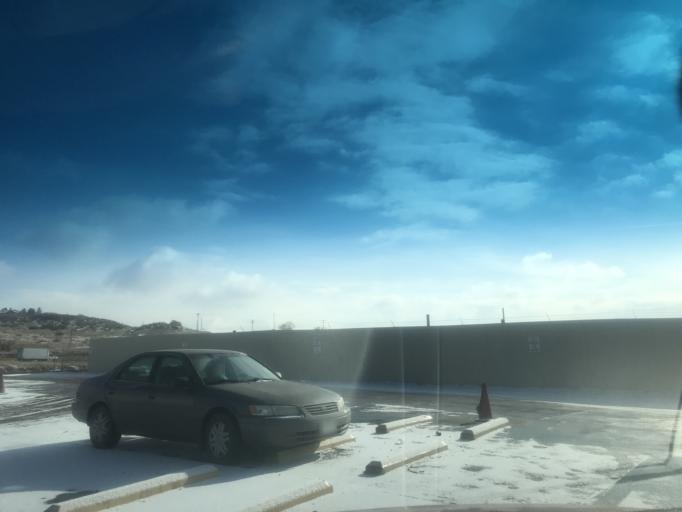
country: US
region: Colorado
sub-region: Douglas County
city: Highlands Ranch
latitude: 39.4870
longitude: -104.9974
